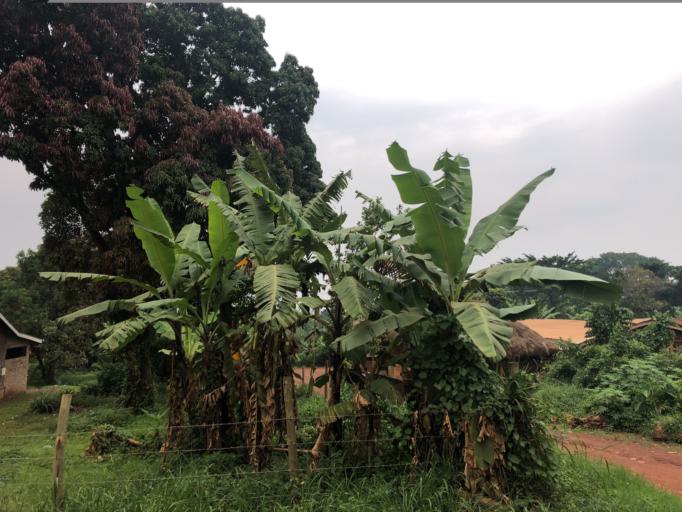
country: UG
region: Central Region
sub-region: Mukono District
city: Mukono
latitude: 0.3587
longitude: 32.7407
